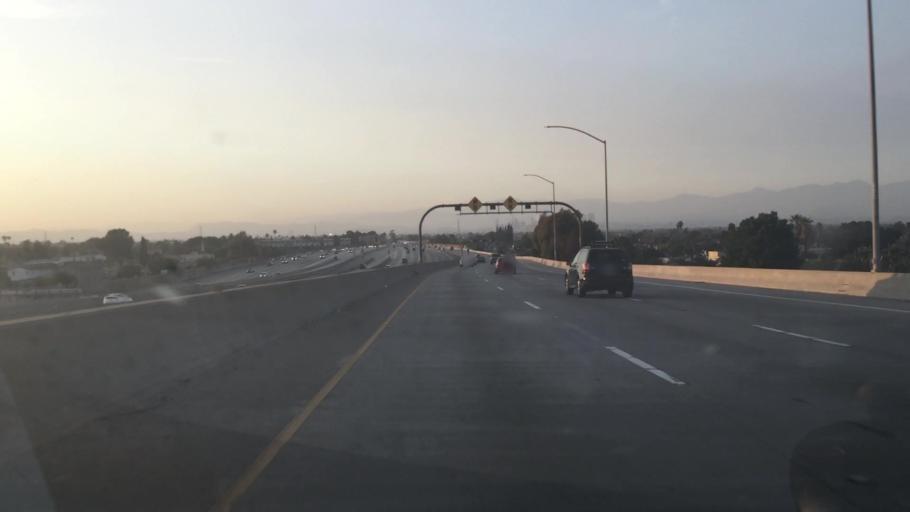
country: US
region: California
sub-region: Los Angeles County
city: Westmont
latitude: 33.9337
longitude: -118.2797
